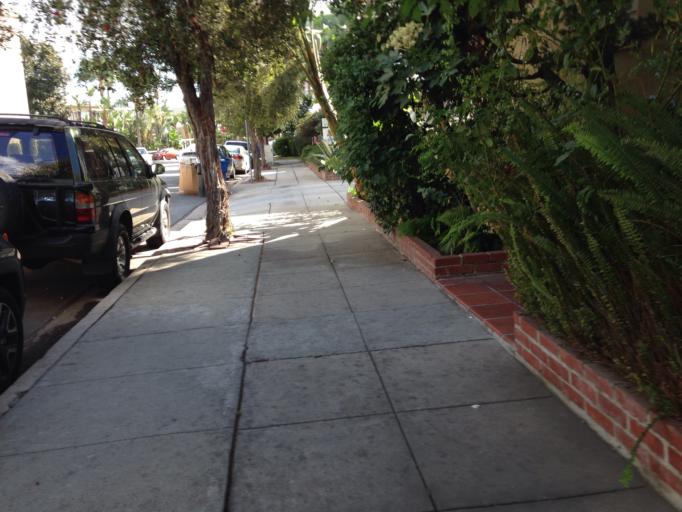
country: US
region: California
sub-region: Los Angeles County
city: Hollywood
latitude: 34.1063
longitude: -118.2978
